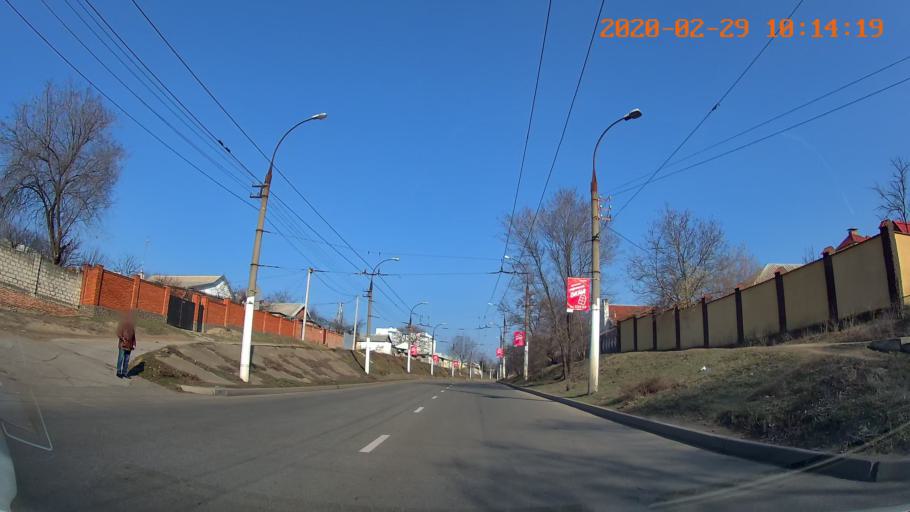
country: MD
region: Telenesti
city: Tiraspolul Nou
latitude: 46.8455
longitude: 29.6438
